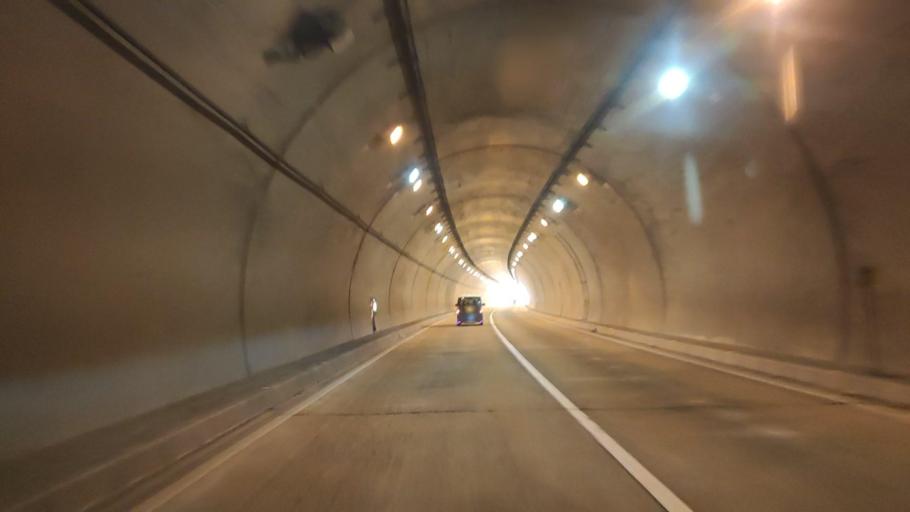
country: JP
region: Fukui
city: Takefu
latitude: 35.8217
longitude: 136.1029
